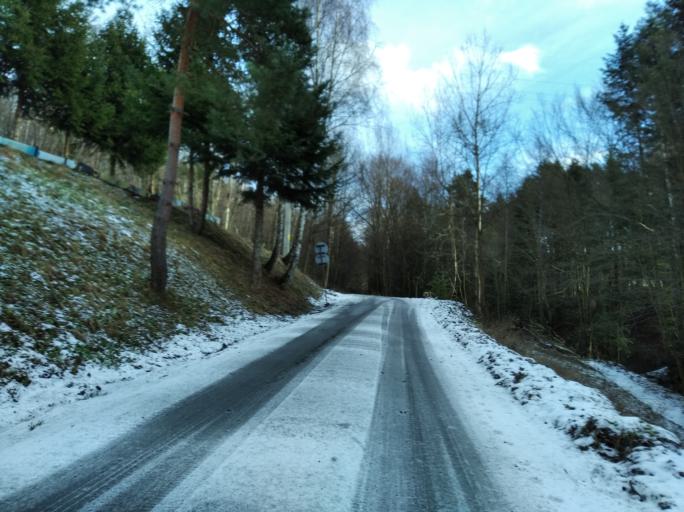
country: PL
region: Subcarpathian Voivodeship
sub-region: Powiat strzyzowski
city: Strzyzow
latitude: 49.9062
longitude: 21.7626
